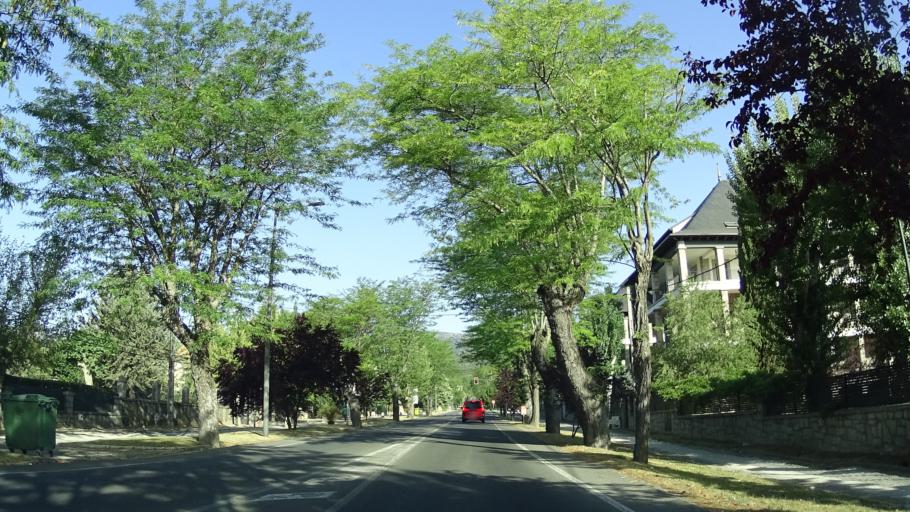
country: ES
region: Madrid
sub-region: Provincia de Madrid
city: Guadarrama
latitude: 40.6748
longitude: -4.0935
